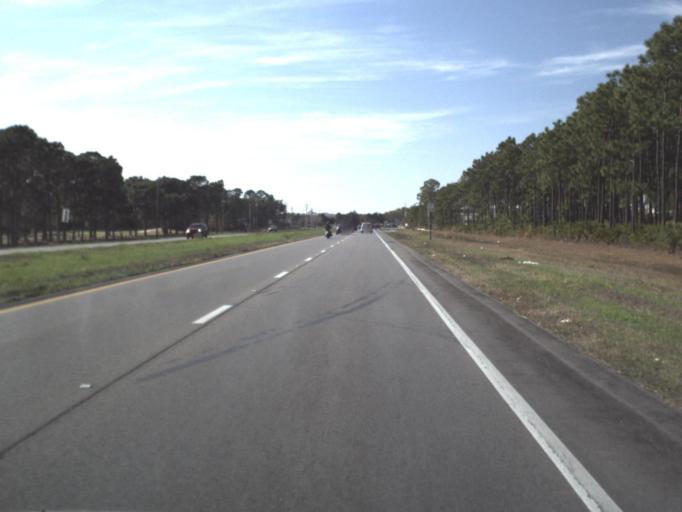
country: US
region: Florida
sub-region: Bay County
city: Panama City Beach
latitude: 30.1940
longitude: -85.8046
